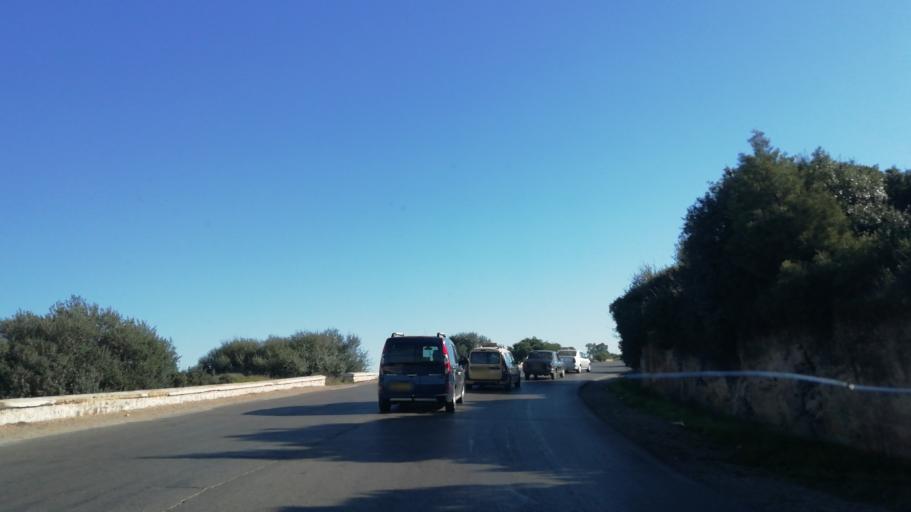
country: DZ
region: Relizane
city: Smala
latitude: 35.7002
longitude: 0.7773
